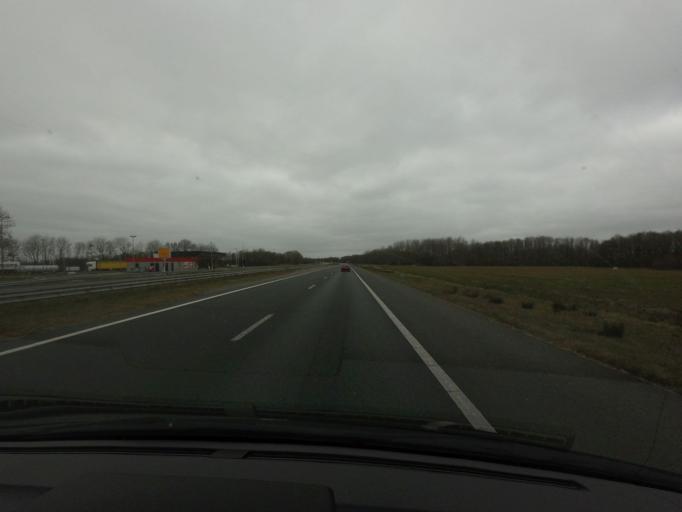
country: NL
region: Groningen
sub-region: Gemeente Hoogezand-Sappemeer
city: Hoogezand
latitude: 53.1944
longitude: 6.7019
